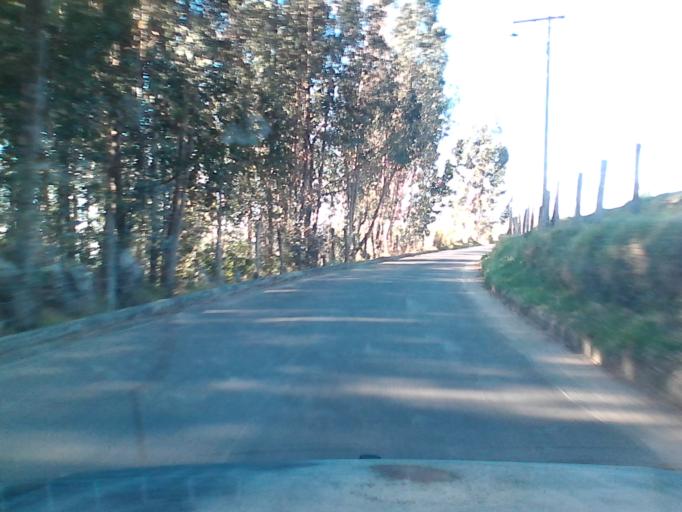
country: CO
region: Boyaca
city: Duitama
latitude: 5.8626
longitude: -73.0329
